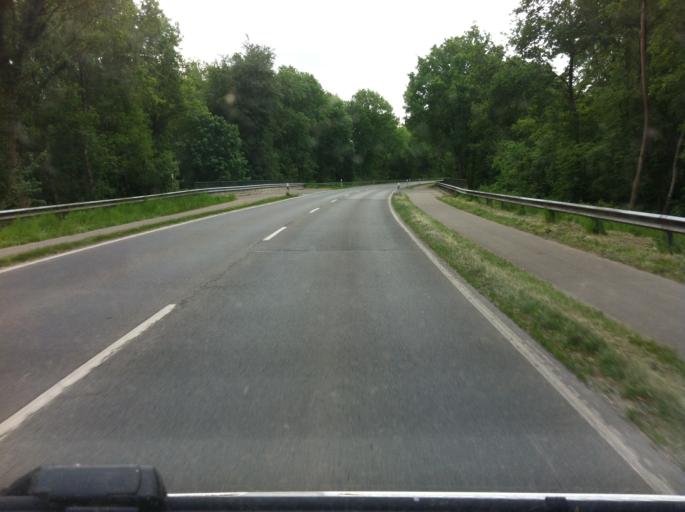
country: DE
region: North Rhine-Westphalia
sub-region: Regierungsbezirk Dusseldorf
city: Bruggen
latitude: 51.2422
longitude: 6.1978
